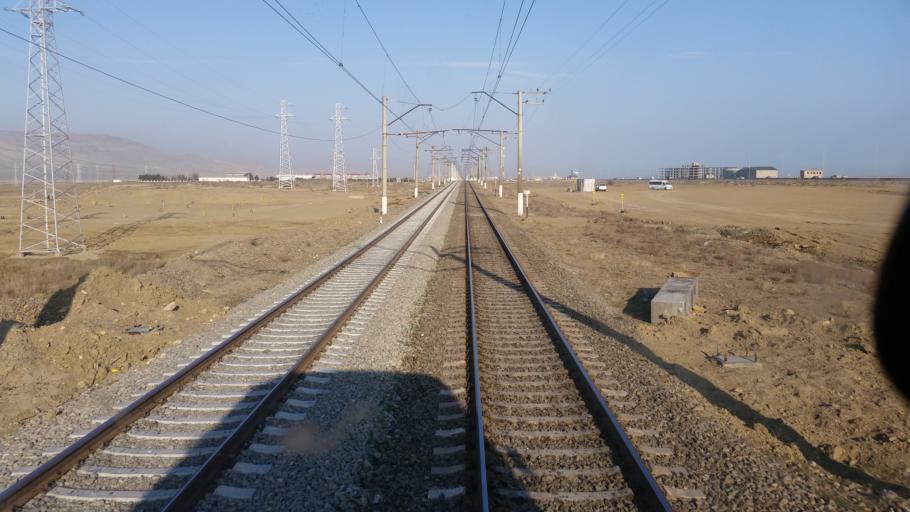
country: AZ
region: Baki
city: Qobustan
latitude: 40.1882
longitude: 49.4917
